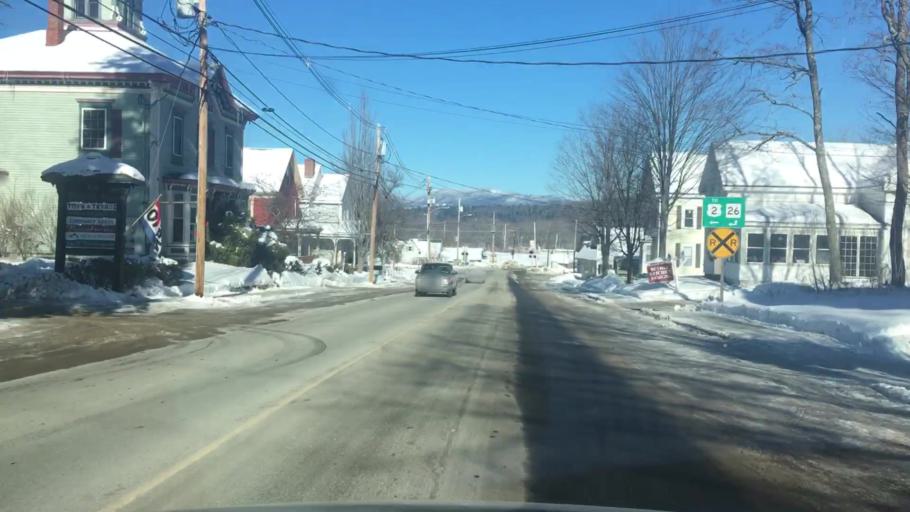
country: US
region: Maine
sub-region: Oxford County
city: Bethel
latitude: 44.4095
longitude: -70.7883
